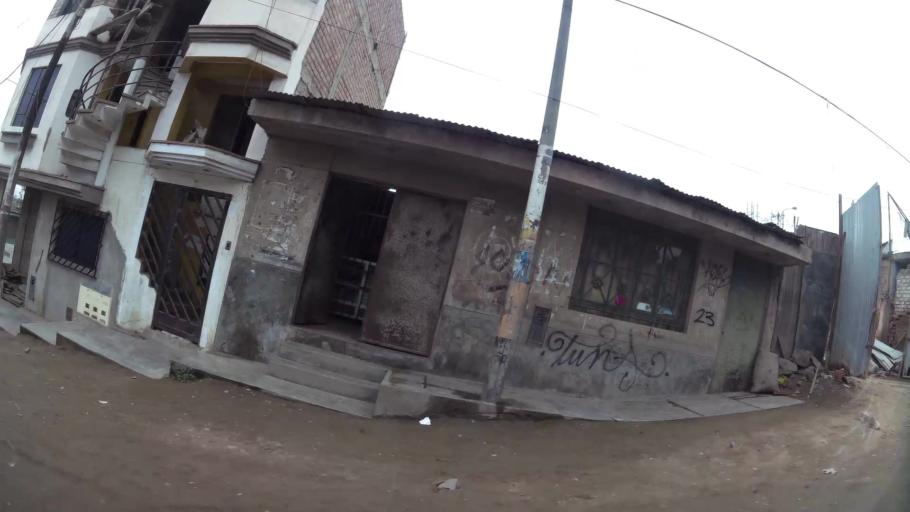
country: PE
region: Lima
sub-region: Lima
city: Surco
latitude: -12.1765
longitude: -76.9575
